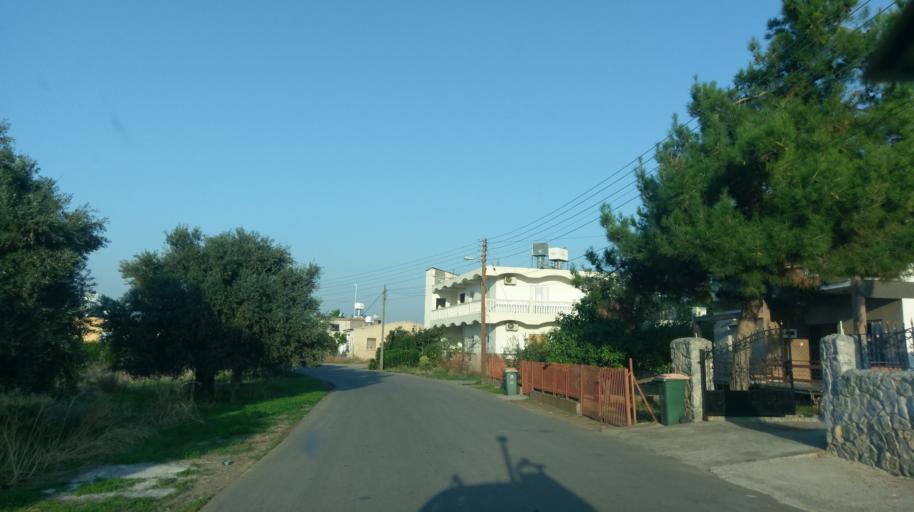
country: CY
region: Lefkosia
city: Morfou
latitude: 35.1632
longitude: 33.0066
